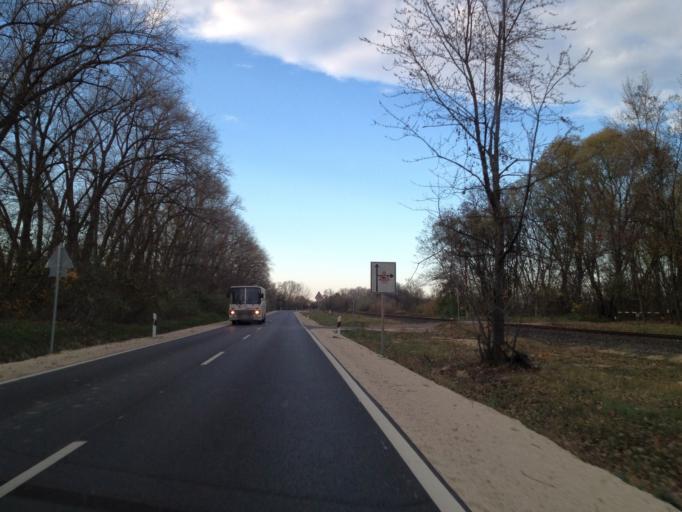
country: HU
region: Gyor-Moson-Sopron
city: Nyul
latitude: 47.6131
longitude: 17.6813
